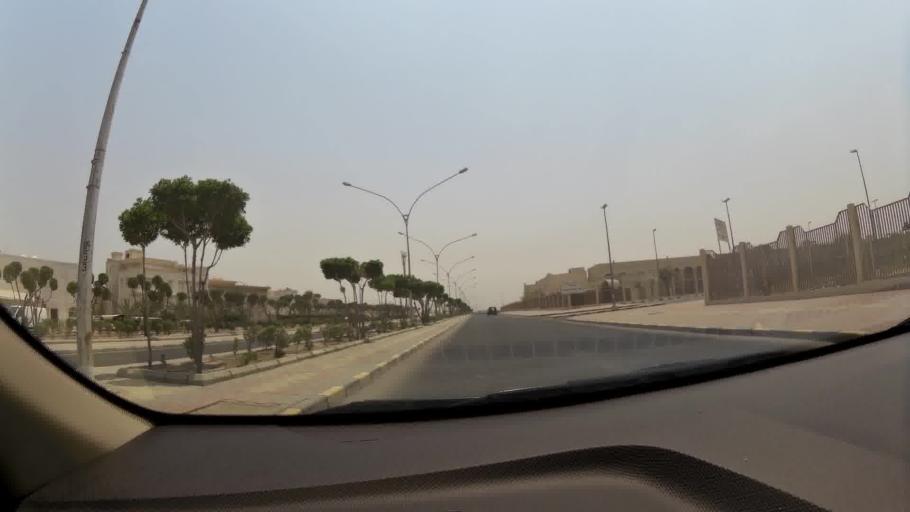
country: KW
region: Al Asimah
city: Ar Rabiyah
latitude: 29.3150
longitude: 47.8189
